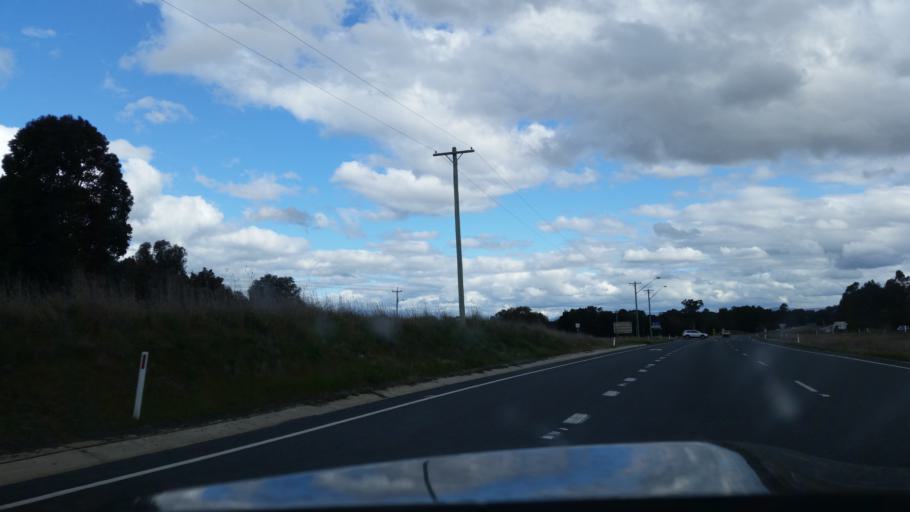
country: AU
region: New South Wales
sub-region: Albury Municipality
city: Lavington
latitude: -35.9708
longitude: 147.0045
